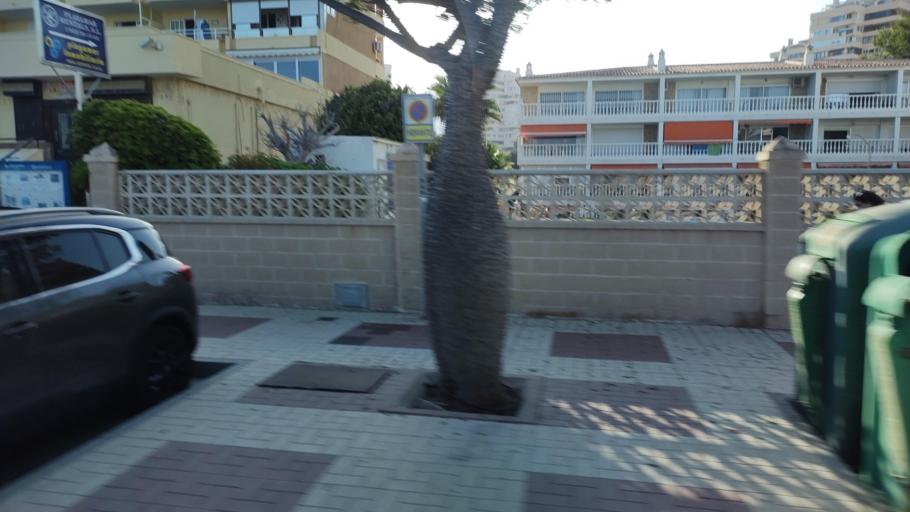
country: ES
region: Andalusia
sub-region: Provincia de Malaga
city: Torremolinos
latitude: 36.6289
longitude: -4.4908
